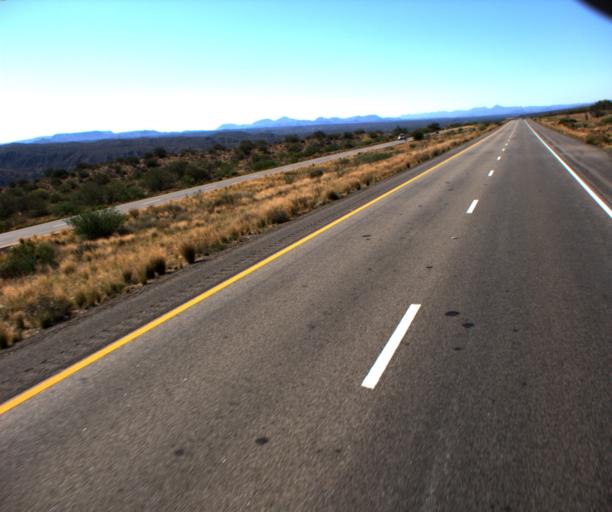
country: US
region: Arizona
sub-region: Mohave County
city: Kingman
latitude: 34.8773
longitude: -113.6473
